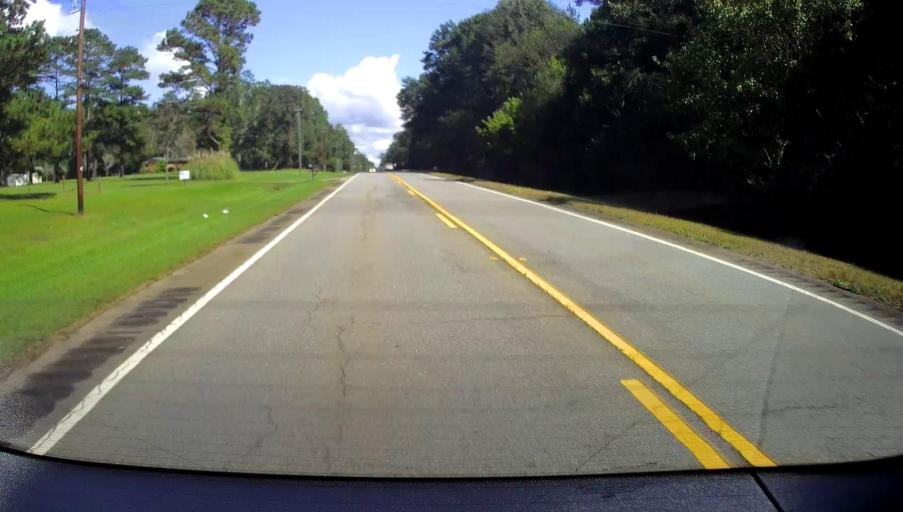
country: US
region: Georgia
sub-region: Jones County
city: Gray
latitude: 33.0308
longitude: -83.4374
